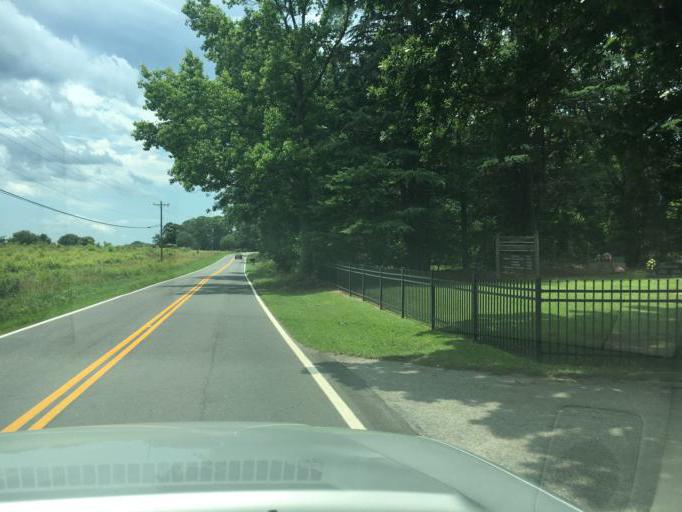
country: US
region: South Carolina
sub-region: Greenville County
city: Greer
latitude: 34.8723
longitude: -82.2061
